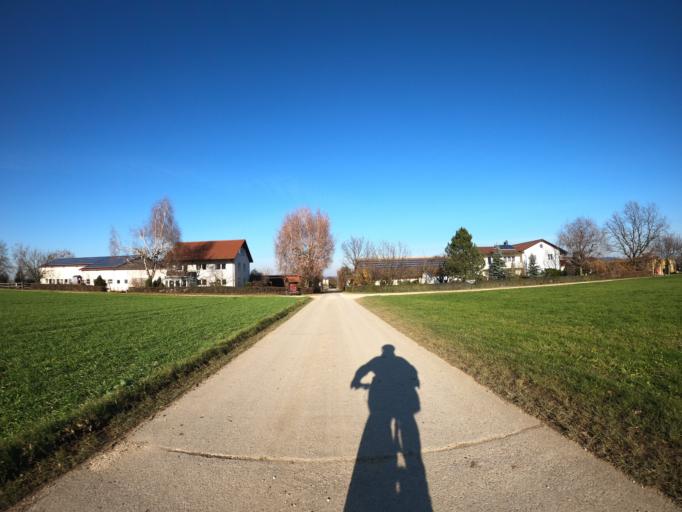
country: DE
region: Baden-Wuerttemberg
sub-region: Regierungsbezirk Stuttgart
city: Gammelshausen
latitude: 48.6480
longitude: 9.6523
